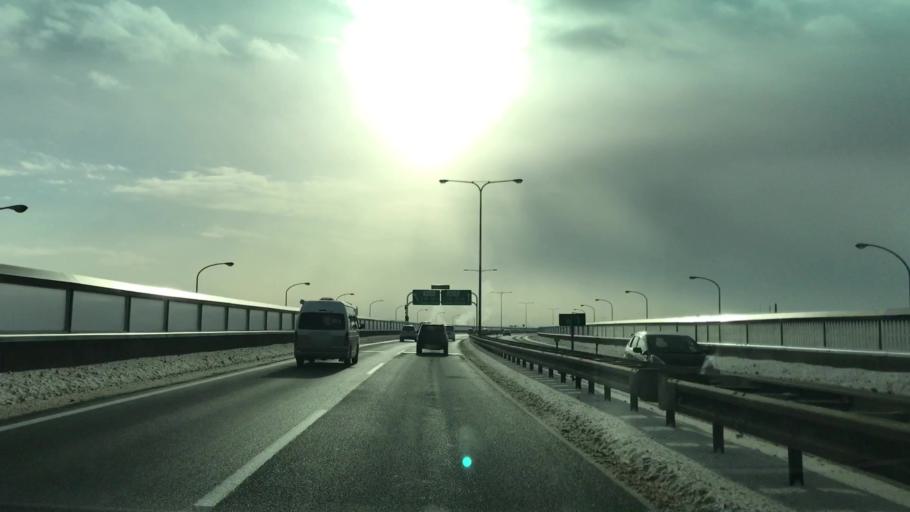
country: JP
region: Hokkaido
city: Sapporo
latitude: 43.0856
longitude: 141.4174
